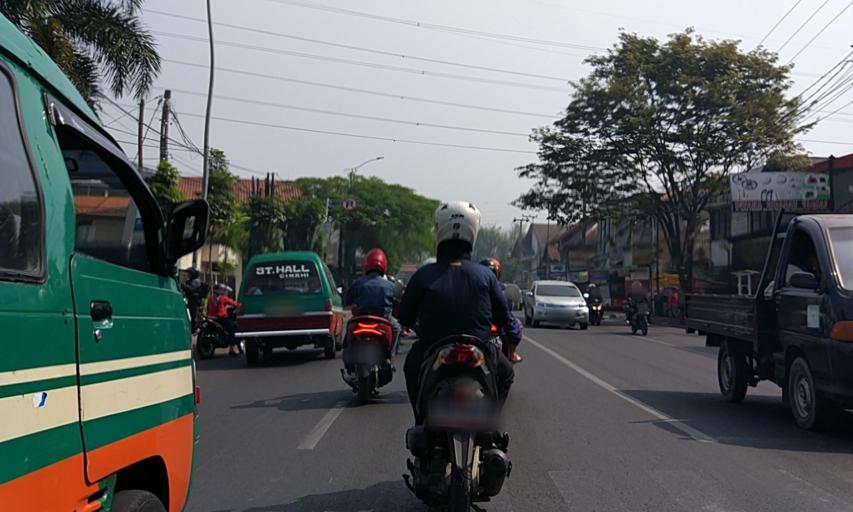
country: ID
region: West Java
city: Cimahi
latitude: -6.8841
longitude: 107.5531
